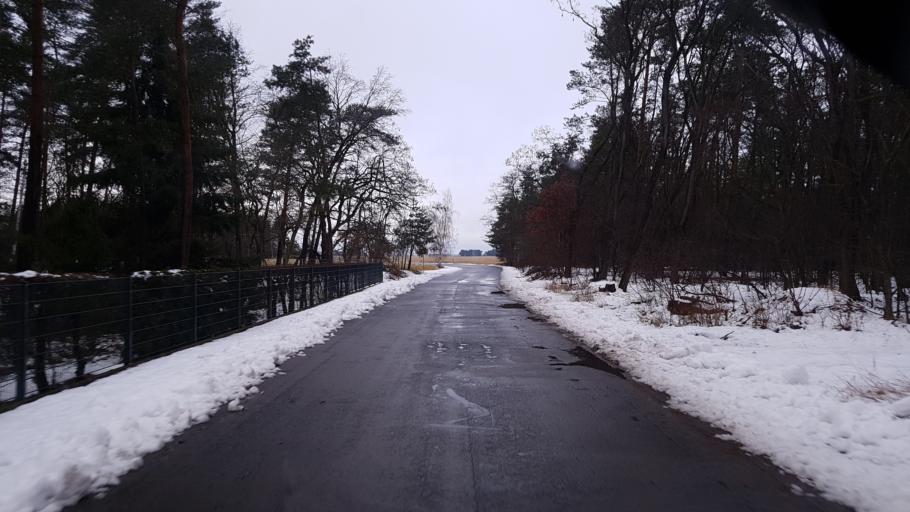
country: DE
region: Brandenburg
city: Luebben
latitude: 51.8639
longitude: 13.8127
